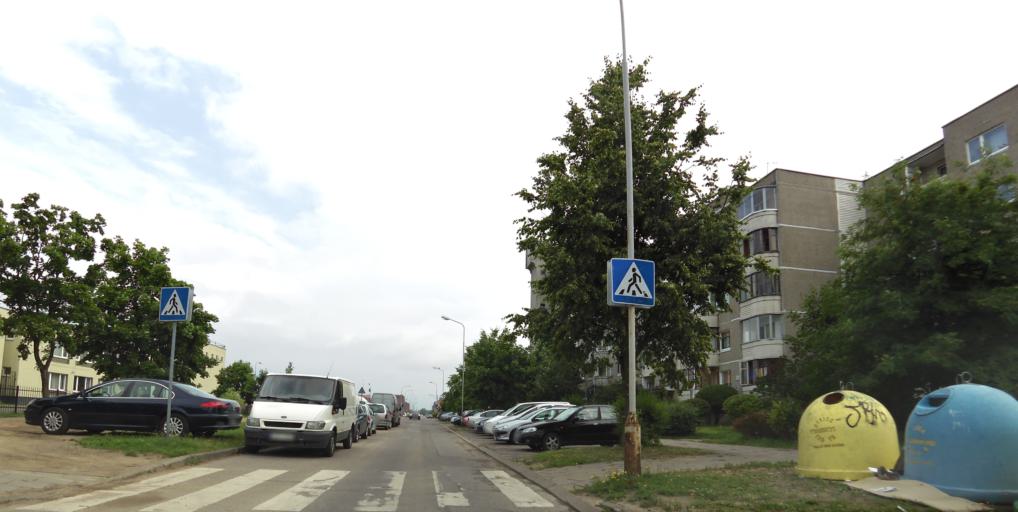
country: LT
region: Vilnius County
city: Pilaite
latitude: 54.7060
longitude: 25.1819
